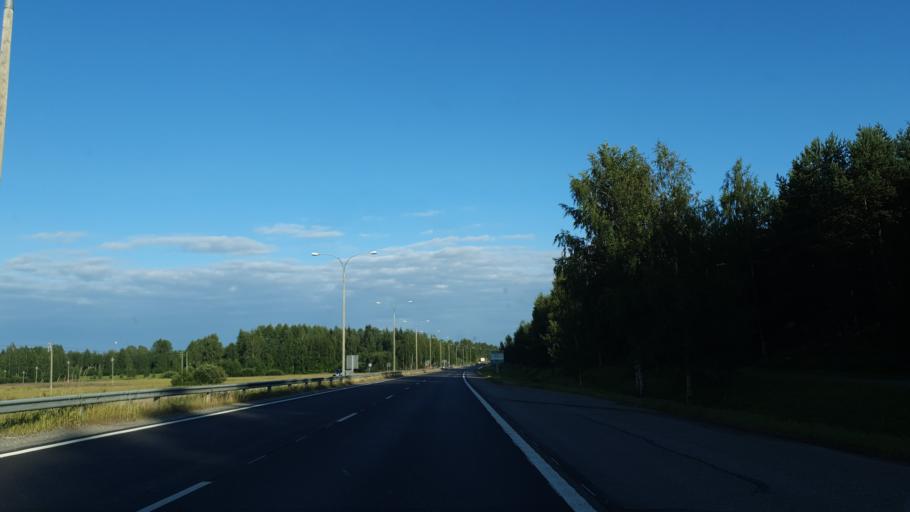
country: FI
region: North Karelia
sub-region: Joensuu
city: Joensuu
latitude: 62.6230
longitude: 29.7168
